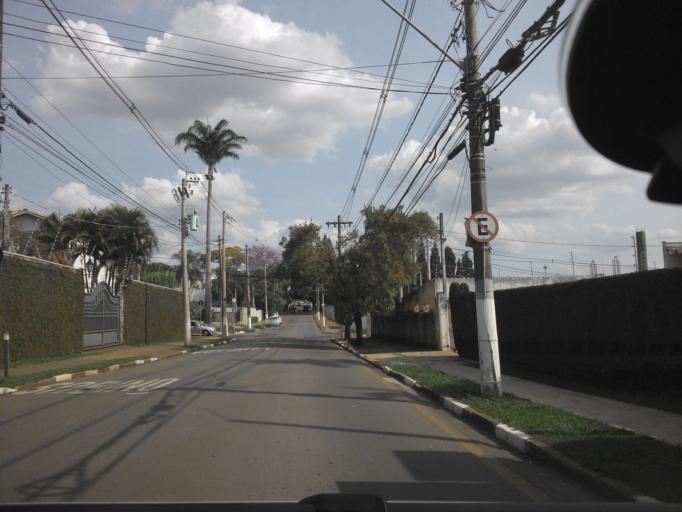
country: BR
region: Sao Paulo
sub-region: Campinas
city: Campinas
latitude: -22.8583
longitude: -47.0528
